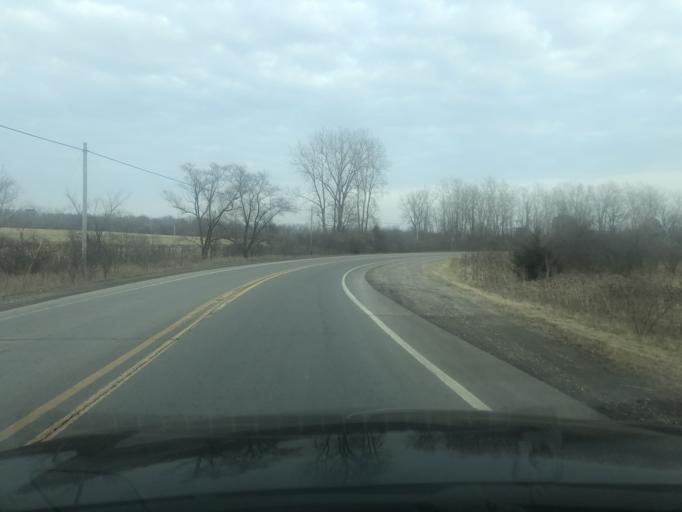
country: US
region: Michigan
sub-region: Wayne County
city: Belleville
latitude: 42.2208
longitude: -83.5469
